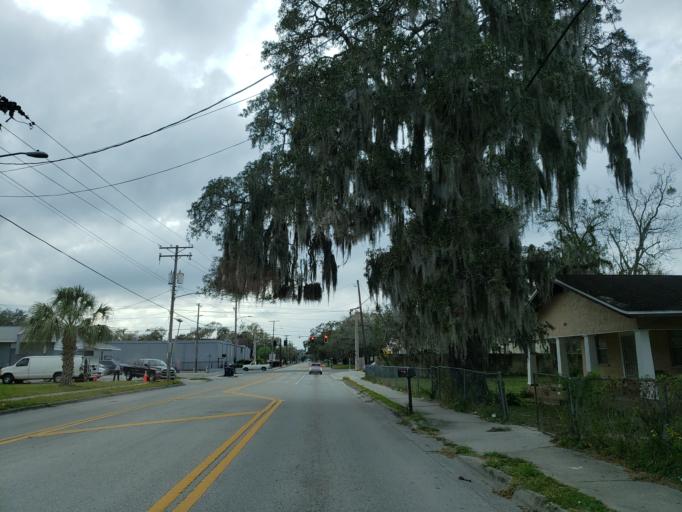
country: US
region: Florida
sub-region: Hillsborough County
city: East Lake-Orient Park
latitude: 27.9778
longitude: -82.4214
